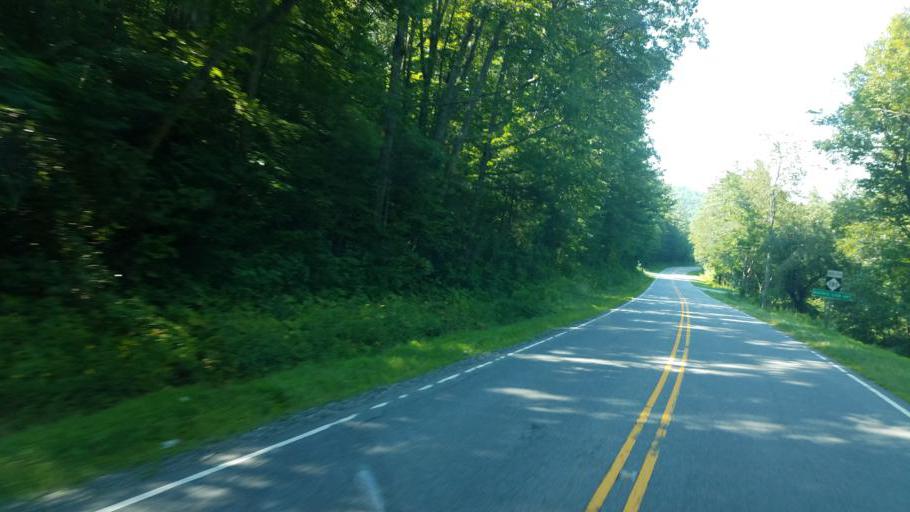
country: US
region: North Carolina
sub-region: Avery County
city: Newland
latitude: 35.9957
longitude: -81.8907
